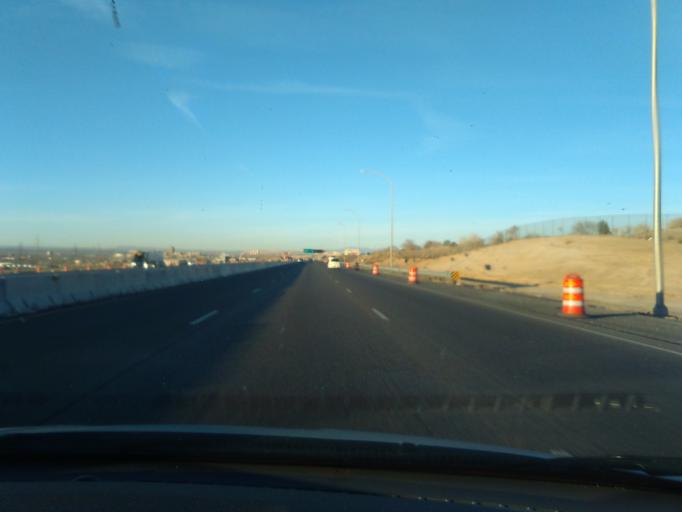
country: US
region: New Mexico
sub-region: Bernalillo County
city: South Valley
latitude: 35.0331
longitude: -106.6380
